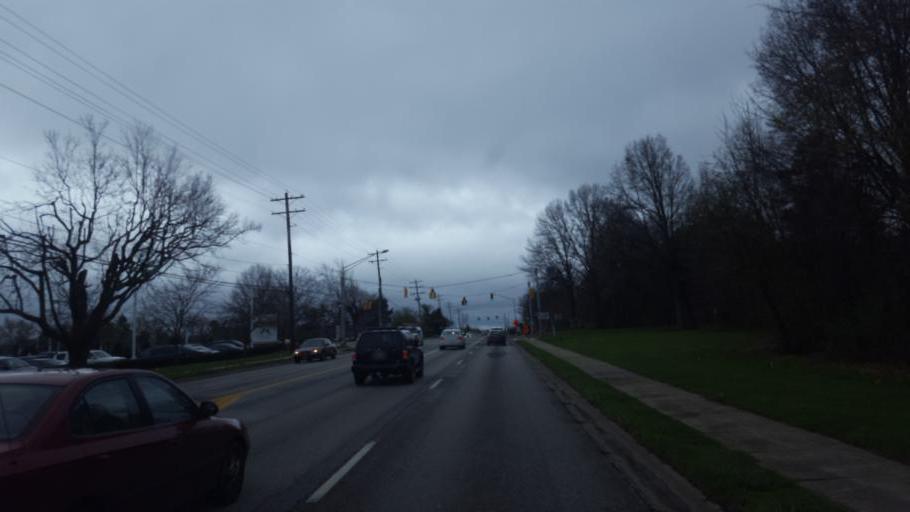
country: US
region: Ohio
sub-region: Franklin County
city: Westerville
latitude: 40.1149
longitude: -82.9490
